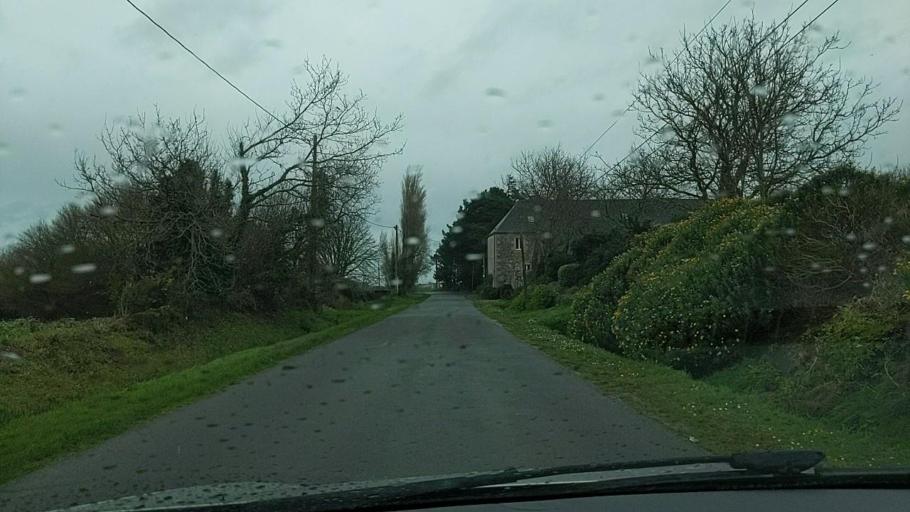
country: FR
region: Brittany
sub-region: Departement des Cotes-d'Armor
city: Pleumeur-Gautier
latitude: 48.8221
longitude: -3.1771
